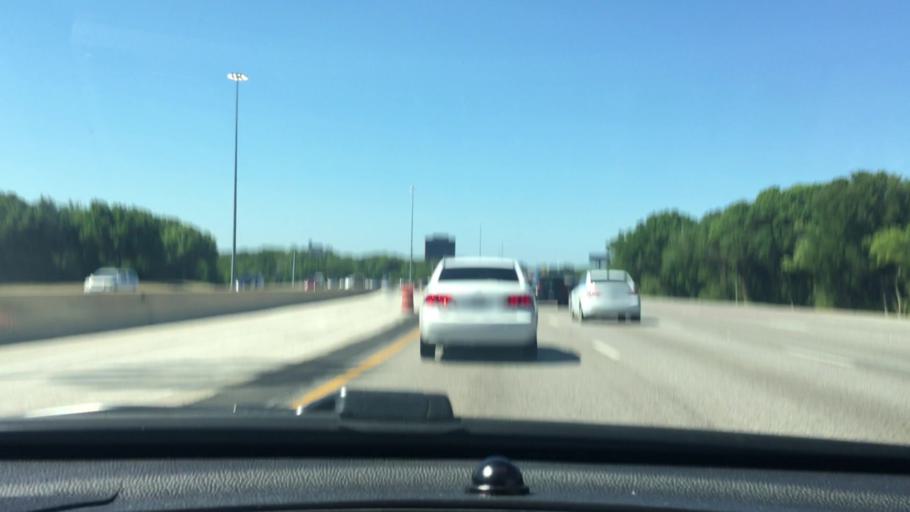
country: US
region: Texas
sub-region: Dallas County
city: Dallas
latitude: 32.7276
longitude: -96.8255
